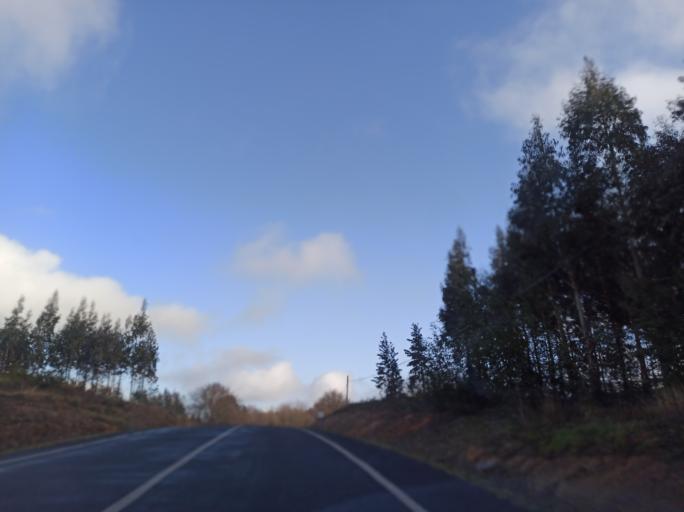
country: ES
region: Galicia
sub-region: Provincia da Coruna
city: Sobrado
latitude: 43.0822
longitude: -8.0035
